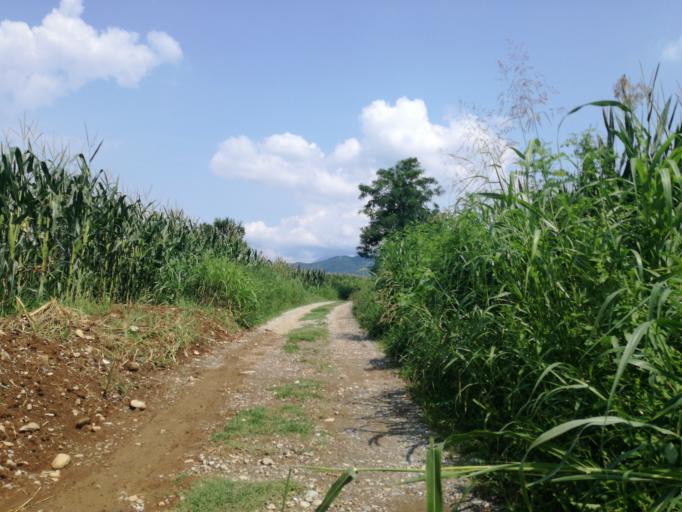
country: IT
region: Lombardy
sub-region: Provincia di Bergamo
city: Calusco d'Adda
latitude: 45.6768
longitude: 9.4743
